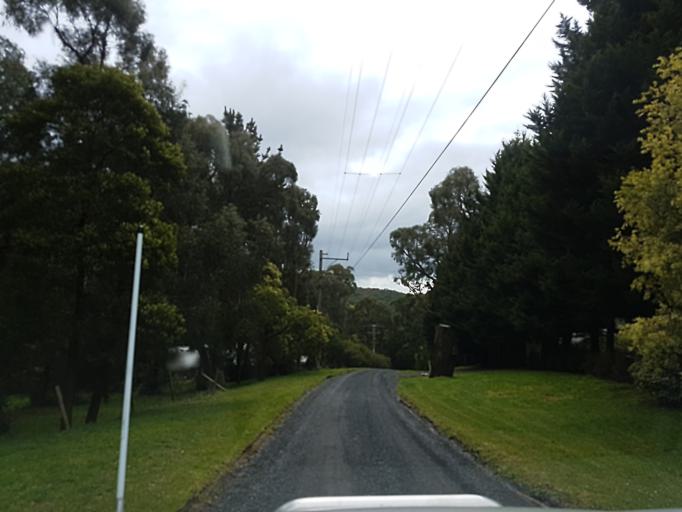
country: AU
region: Victoria
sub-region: Cardinia
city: Emerald
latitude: -37.8966
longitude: 145.4352
